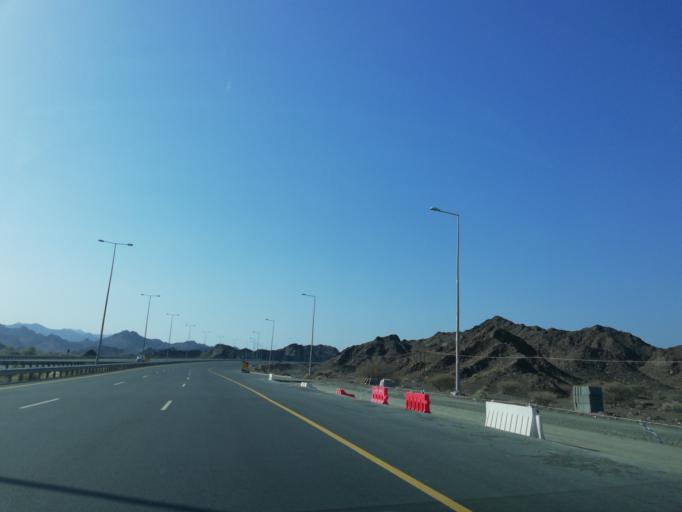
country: OM
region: Muhafazat ad Dakhiliyah
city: Sufalat Sama'il
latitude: 23.0070
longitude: 58.2270
